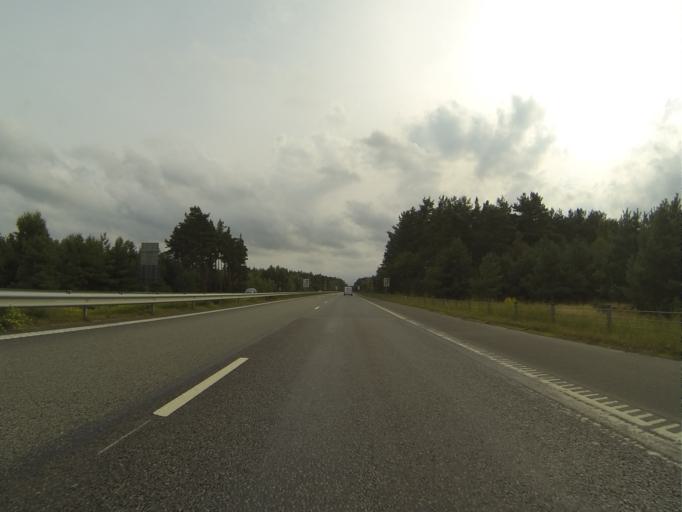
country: SE
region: Skane
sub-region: Kristianstads Kommun
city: Norra Asum
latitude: 55.9846
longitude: 14.0893
